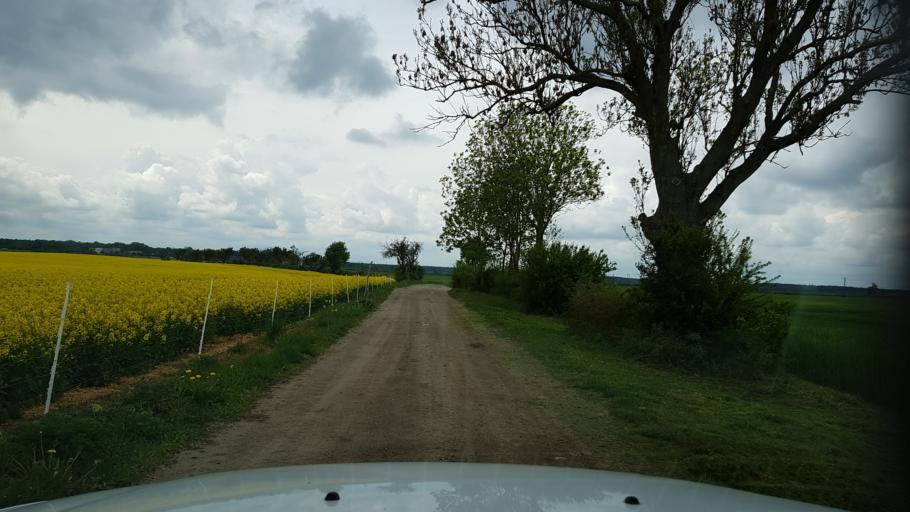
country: PL
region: West Pomeranian Voivodeship
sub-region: Powiat gryfinski
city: Mieszkowice
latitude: 52.8398
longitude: 14.4681
